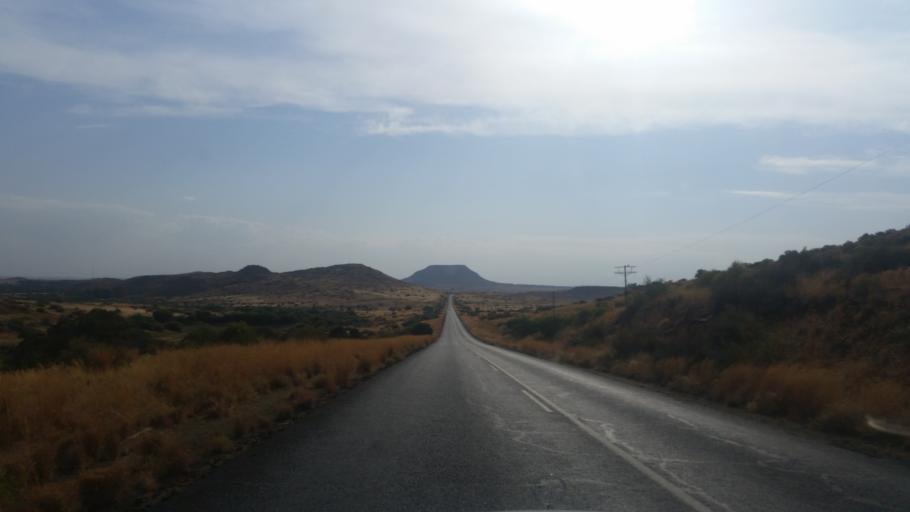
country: ZA
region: Orange Free State
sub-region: Xhariep District Municipality
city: Trompsburg
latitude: -30.4770
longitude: 26.0080
